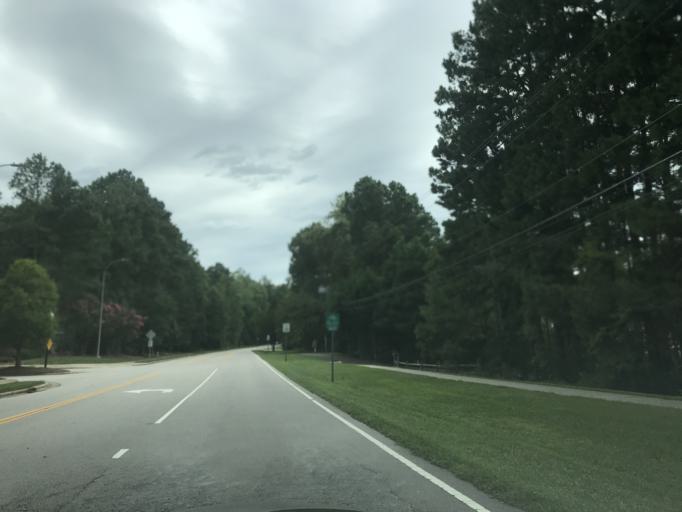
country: US
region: North Carolina
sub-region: Wake County
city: Apex
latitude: 35.7482
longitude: -78.8152
